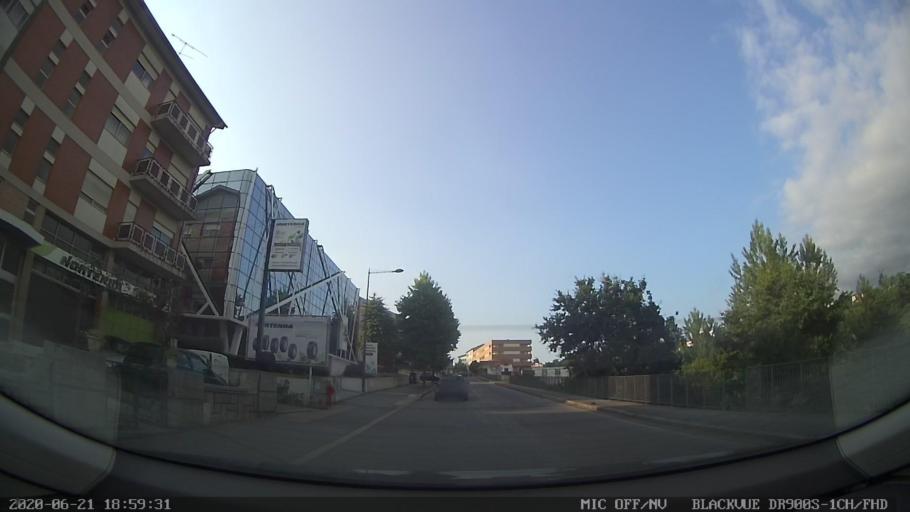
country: PT
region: Porto
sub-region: Amarante
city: Amarante
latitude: 41.2768
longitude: -8.0821
